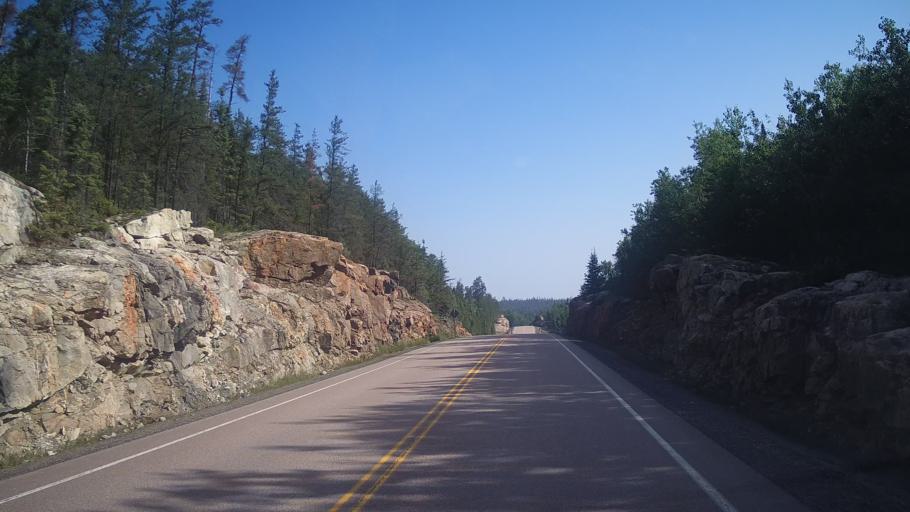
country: CA
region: Ontario
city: Rayside-Balfour
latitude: 46.9838
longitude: -81.6346
